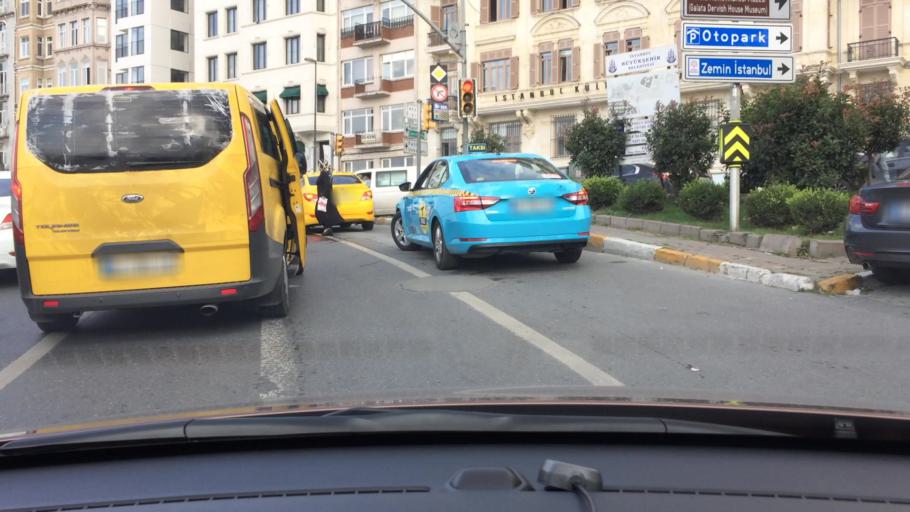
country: TR
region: Istanbul
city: Eminoenue
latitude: 41.0283
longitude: 28.9714
